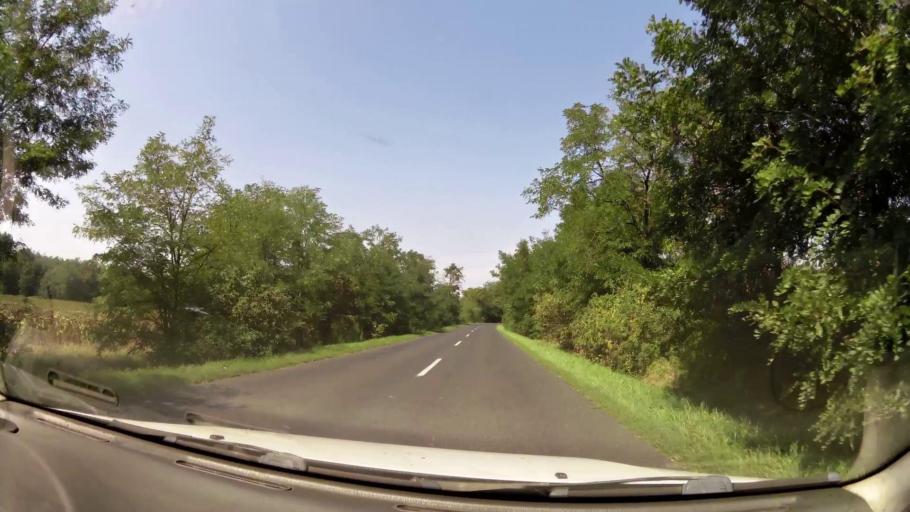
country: HU
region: Pest
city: Tapiosag
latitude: 47.4111
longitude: 19.6124
